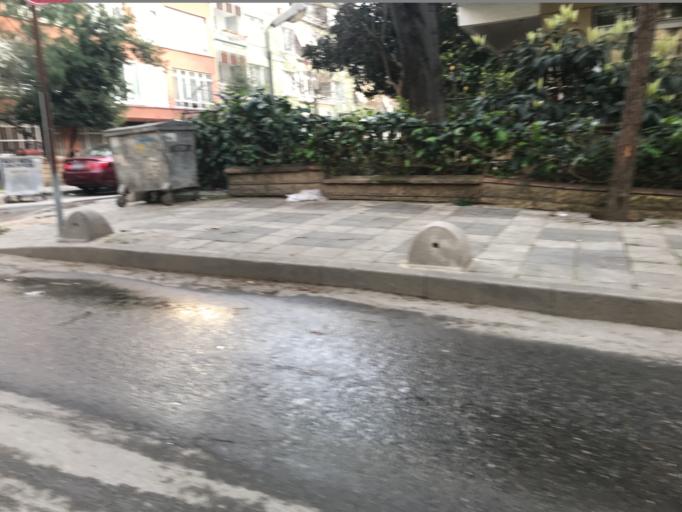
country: TR
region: Istanbul
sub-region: Atasehir
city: Atasehir
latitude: 40.9606
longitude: 29.0926
